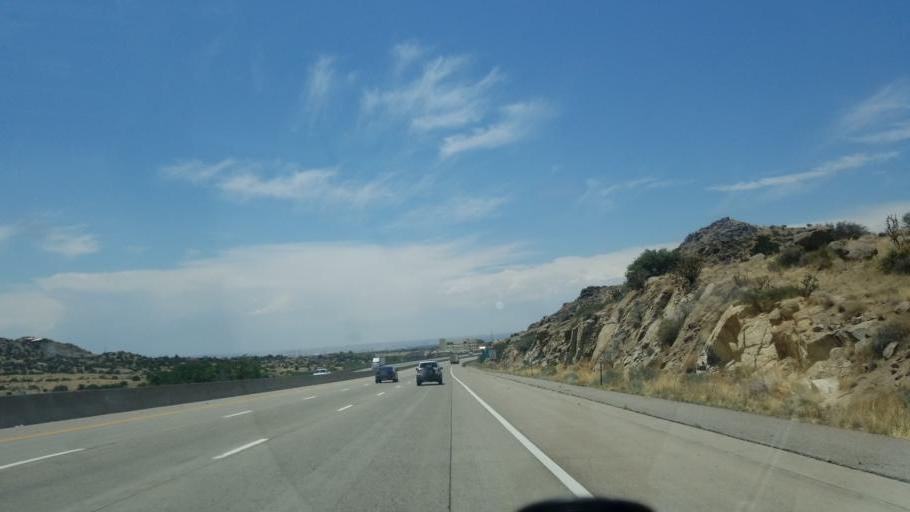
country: US
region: New Mexico
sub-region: Bernalillo County
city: Carnuel
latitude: 35.0631
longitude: -106.4747
